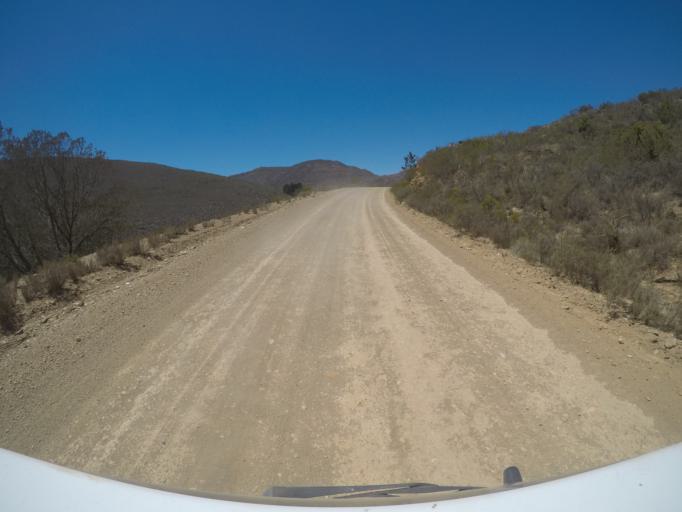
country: ZA
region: Western Cape
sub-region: Overberg District Municipality
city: Grabouw
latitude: -34.1132
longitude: 19.2307
